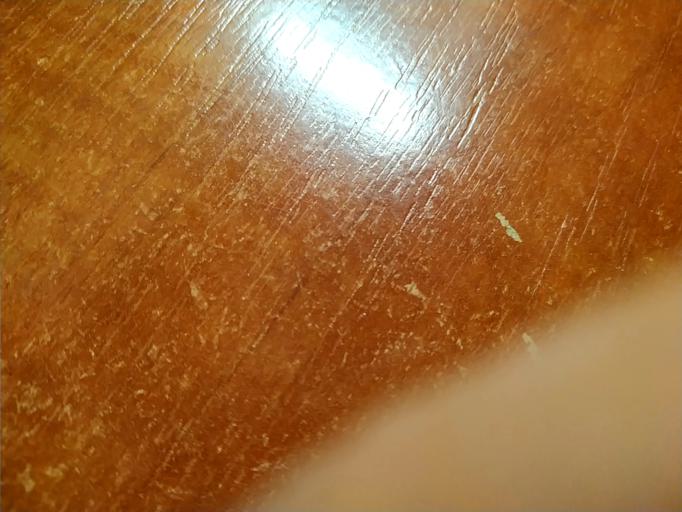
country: RU
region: Kaluga
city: Babynino
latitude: 54.4619
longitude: 35.5382
